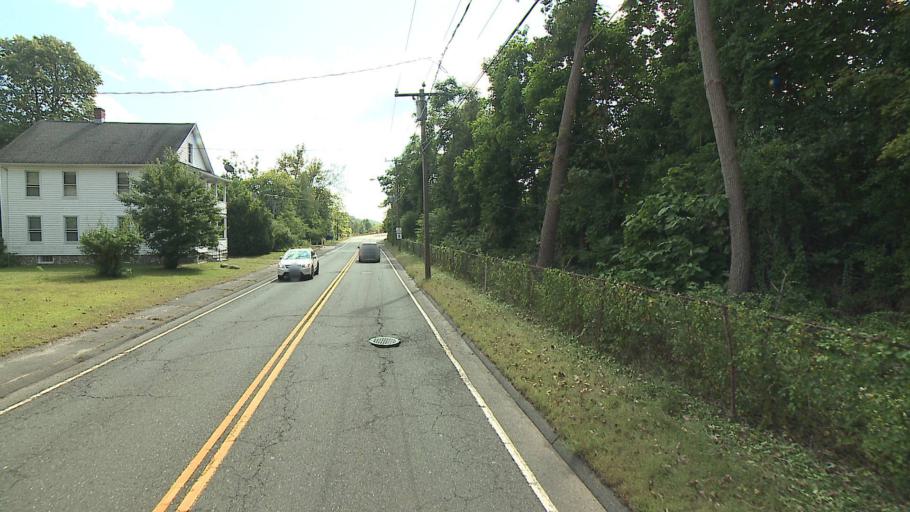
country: US
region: Connecticut
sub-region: New Haven County
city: Seymour
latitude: 41.3839
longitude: -73.0778
